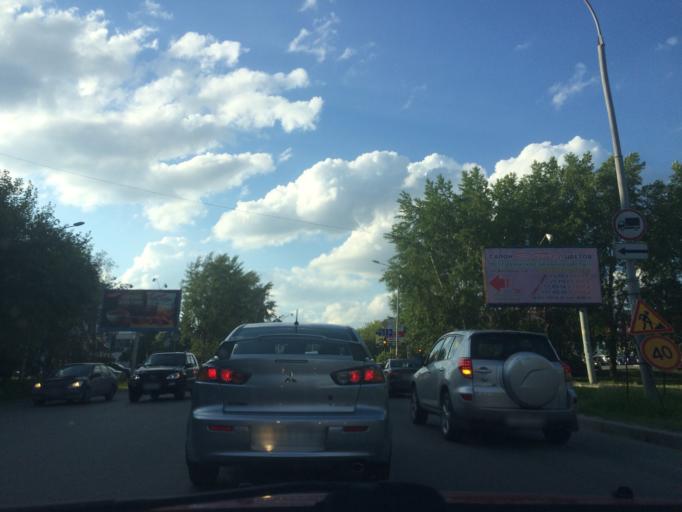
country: RU
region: Sverdlovsk
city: Yekaterinburg
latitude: 56.8205
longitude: 60.6398
